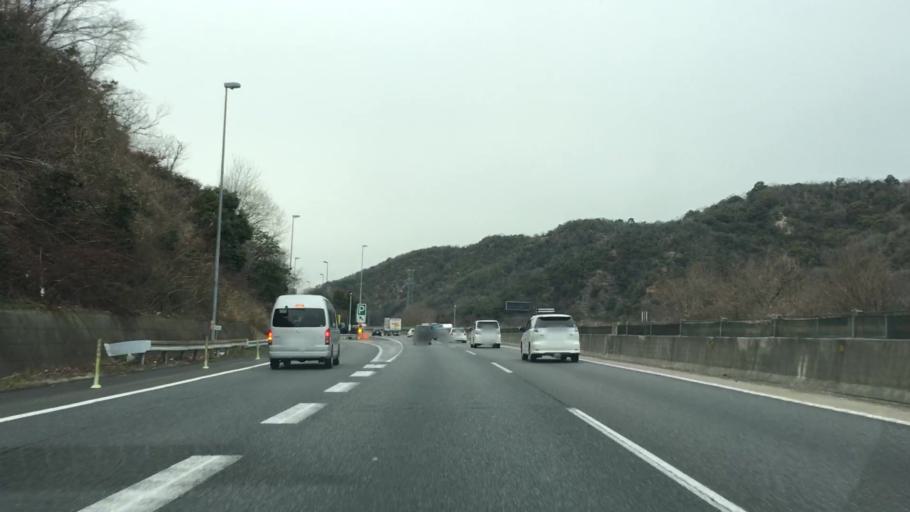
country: JP
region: Aichi
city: Okazaki
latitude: 34.9191
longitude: 137.2371
